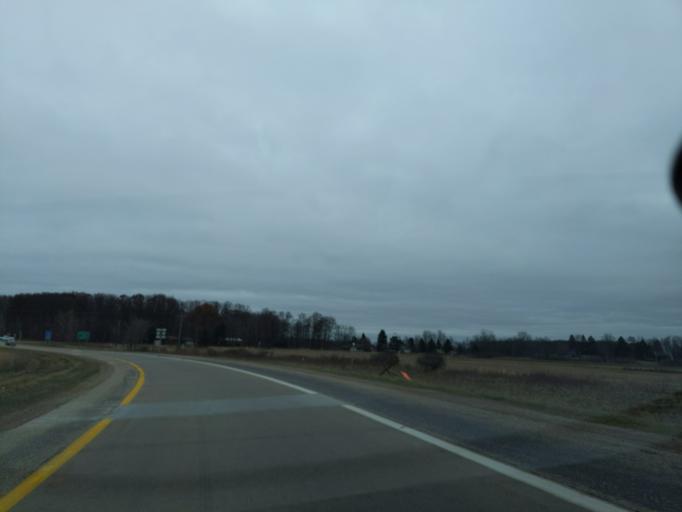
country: US
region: Michigan
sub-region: Clinton County
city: Saint Johns
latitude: 42.9992
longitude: -84.5162
